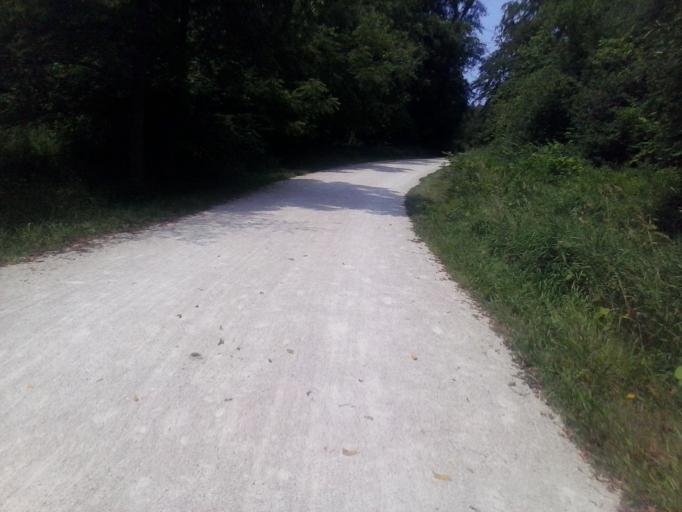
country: US
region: Illinois
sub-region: DuPage County
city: Naperville
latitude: 41.8119
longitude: -88.1430
